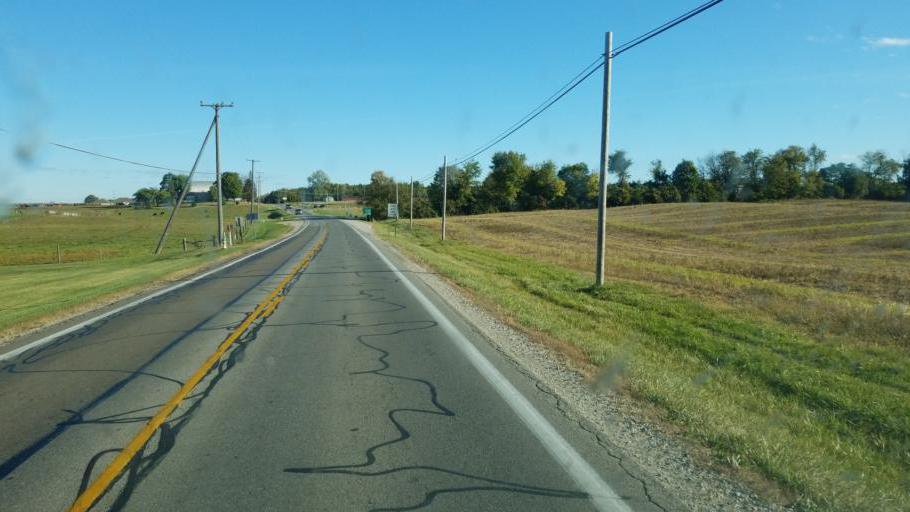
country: US
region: Ohio
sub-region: Morrow County
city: Mount Gilead
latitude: 40.5621
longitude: -82.8252
